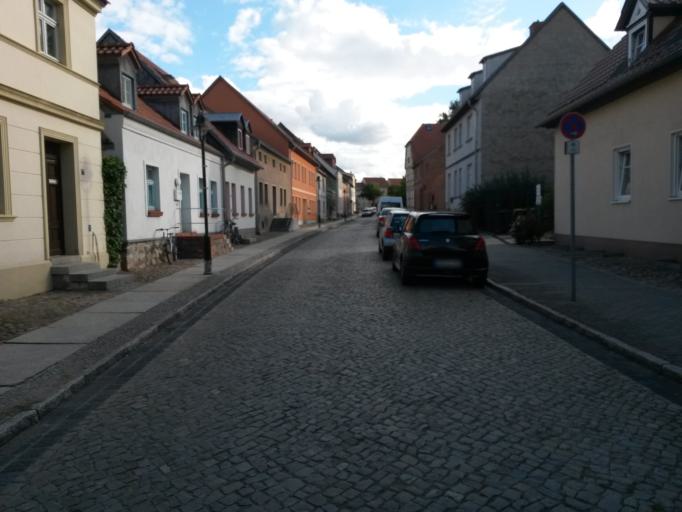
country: DE
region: Brandenburg
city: Angermunde
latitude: 53.0194
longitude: 14.0055
